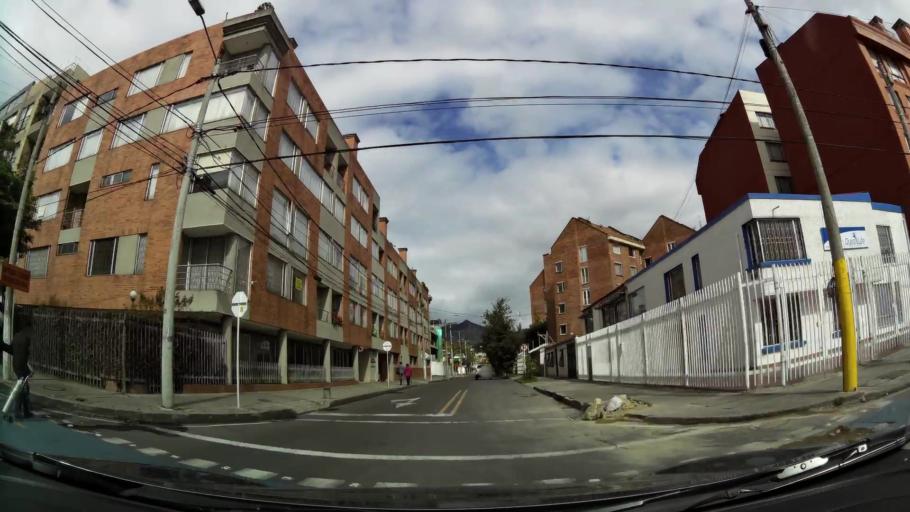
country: CO
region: Bogota D.C.
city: Barrio San Luis
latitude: 4.6899
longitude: -74.0614
